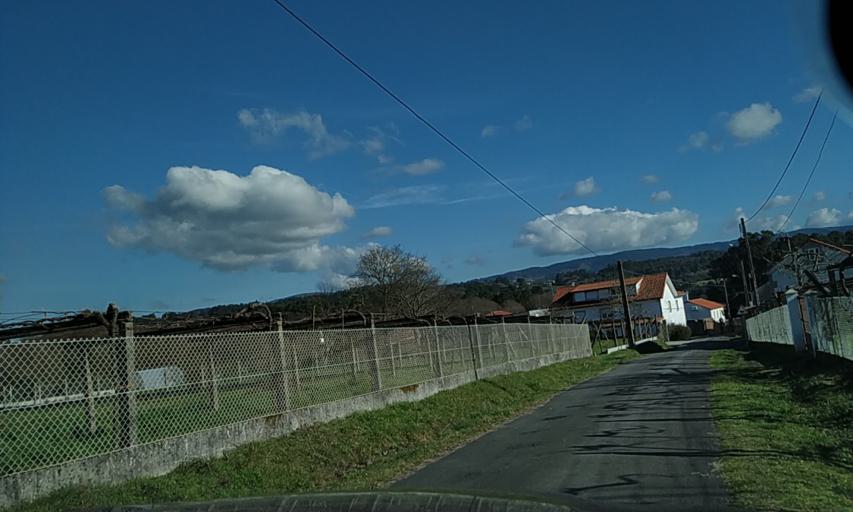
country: ES
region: Galicia
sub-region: Provincia da Coruna
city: Ribeira
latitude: 42.7105
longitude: -8.4466
